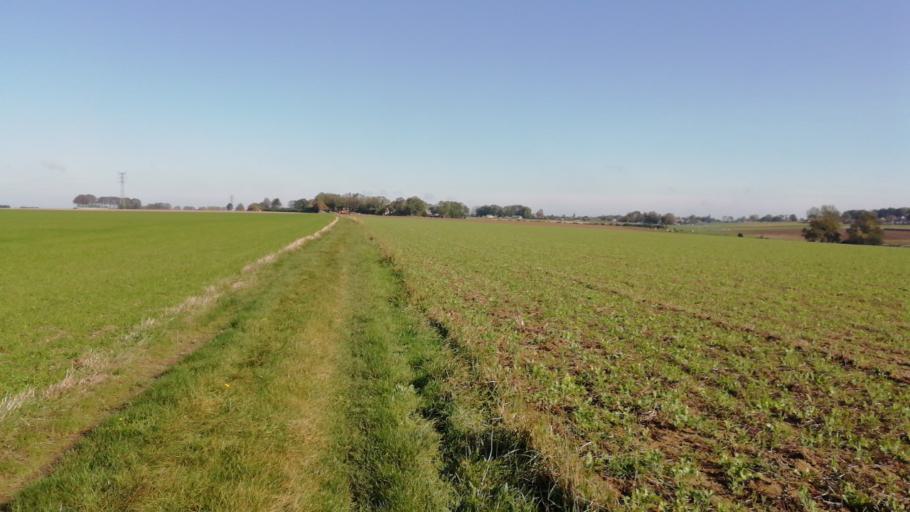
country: FR
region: Haute-Normandie
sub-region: Departement de la Seine-Maritime
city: Maneglise
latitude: 49.5796
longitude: 0.2625
